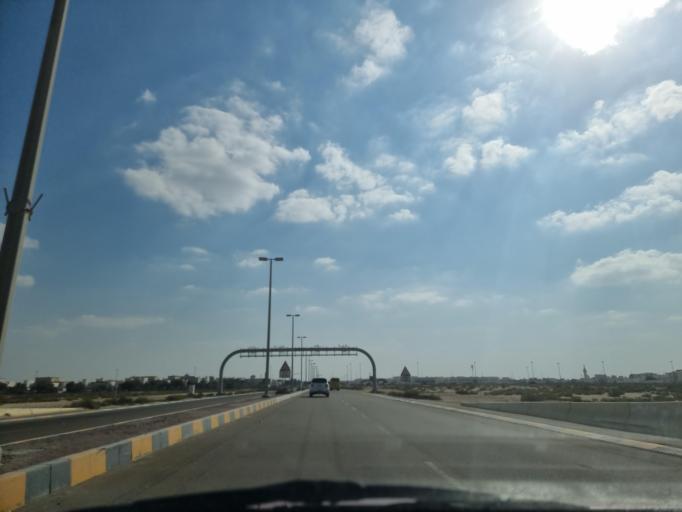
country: AE
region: Abu Dhabi
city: Abu Dhabi
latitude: 24.4159
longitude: 54.7323
